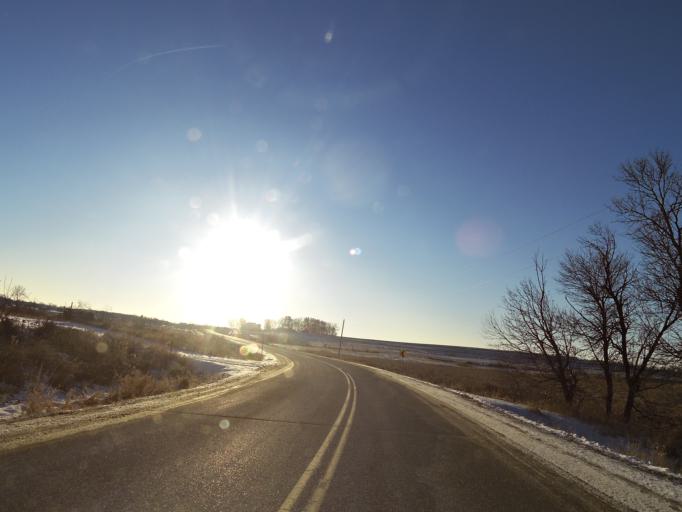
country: US
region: Minnesota
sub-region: Scott County
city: Jordan
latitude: 44.6598
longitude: -93.5314
